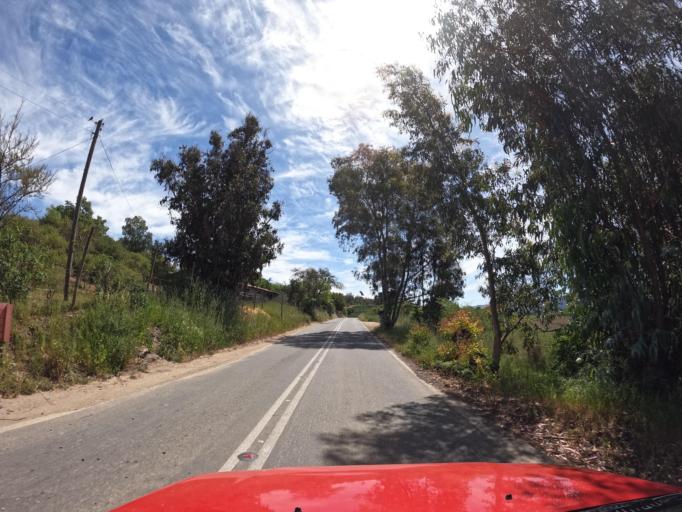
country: CL
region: Maule
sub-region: Provincia de Talca
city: Talca
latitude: -35.0054
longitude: -71.7902
